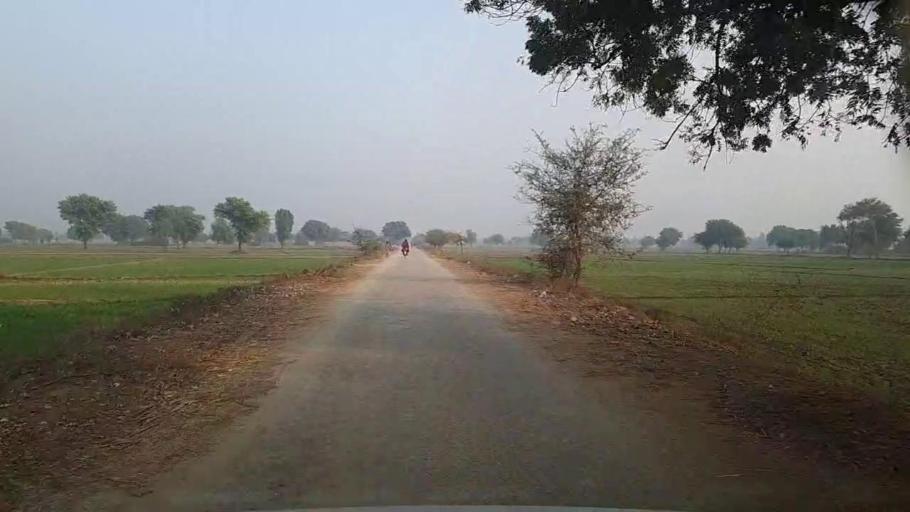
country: PK
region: Sindh
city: Bozdar
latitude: 27.0810
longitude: 68.5717
